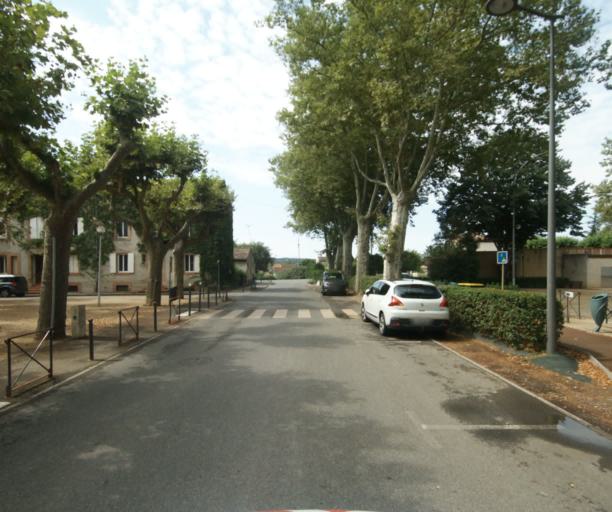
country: FR
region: Midi-Pyrenees
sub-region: Departement de la Haute-Garonne
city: Revel
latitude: 43.4617
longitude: 1.9995
